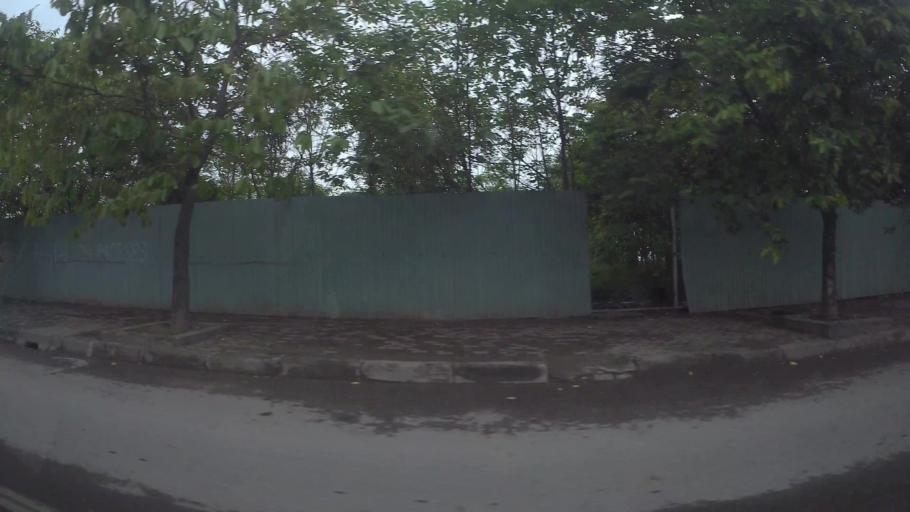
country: VN
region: Ha Noi
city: Van Dien
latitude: 20.9656
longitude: 105.8534
